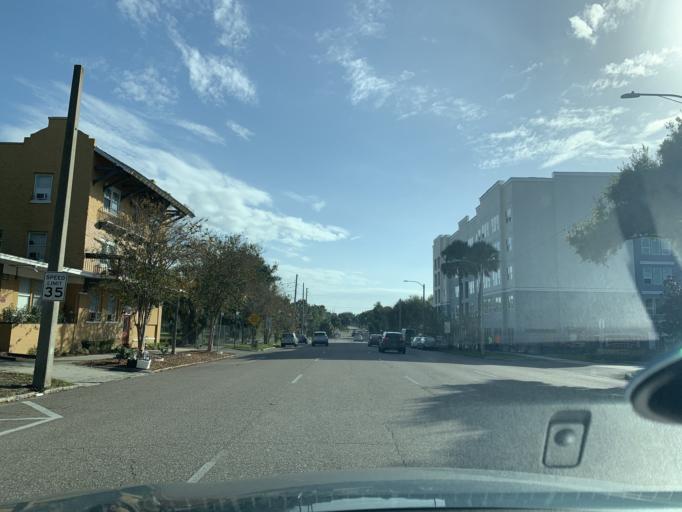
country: US
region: Florida
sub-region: Pinellas County
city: Saint Petersburg
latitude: 27.7654
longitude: -82.6466
